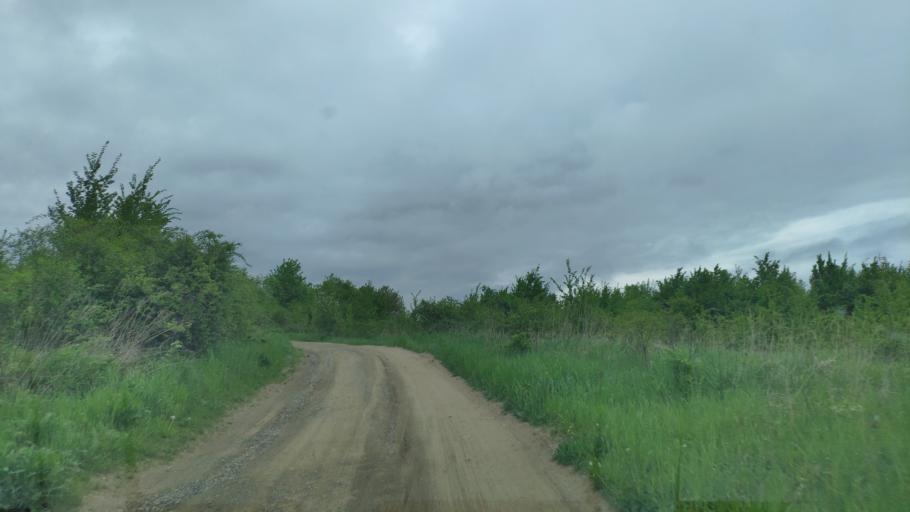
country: SK
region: Kosicky
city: Kosice
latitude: 48.7620
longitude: 21.2023
